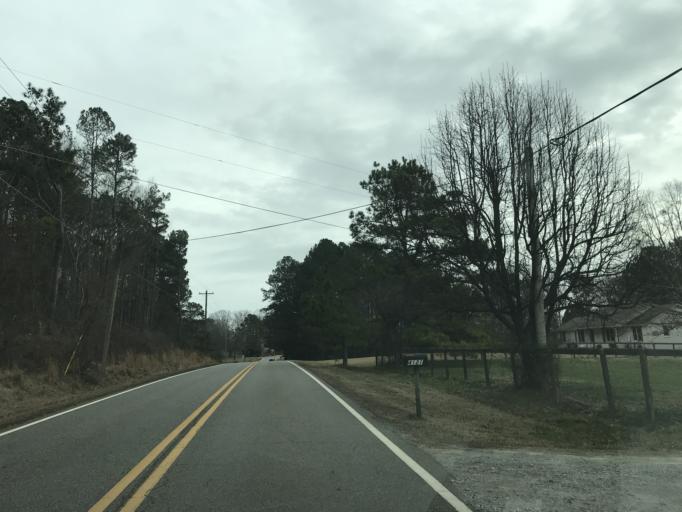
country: US
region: Georgia
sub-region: Fulton County
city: Milton
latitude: 34.1959
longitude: -84.3461
